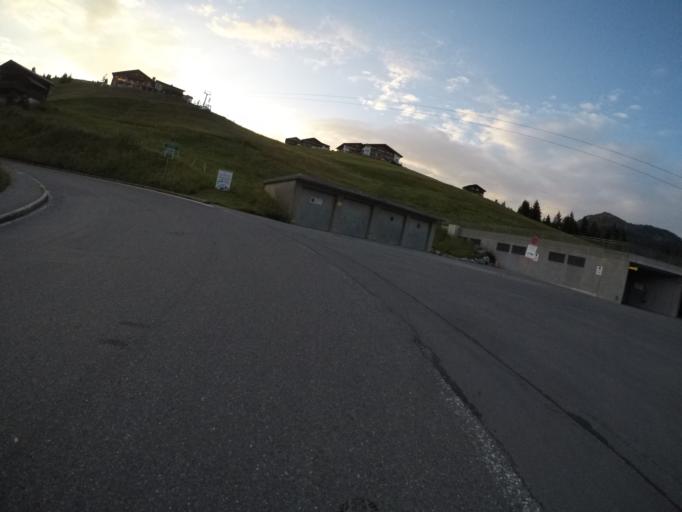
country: AT
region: Vorarlberg
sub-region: Politischer Bezirk Bregenz
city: Damuels
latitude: 47.2818
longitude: 9.8838
